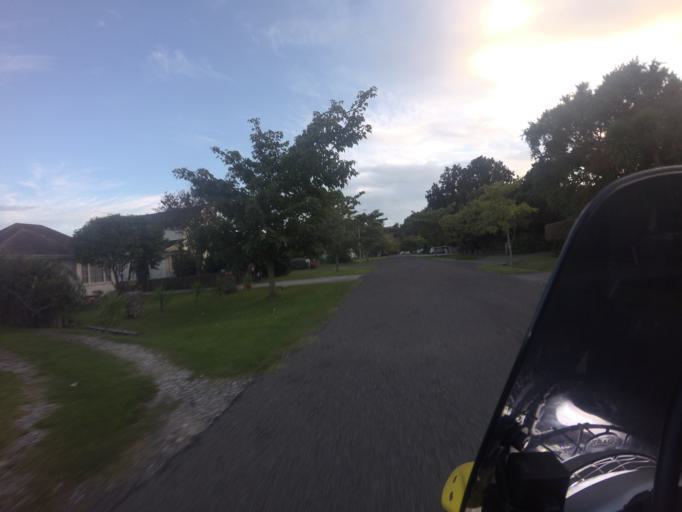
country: NZ
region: Gisborne
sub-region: Gisborne District
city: Gisborne
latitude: -38.6644
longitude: 178.0371
